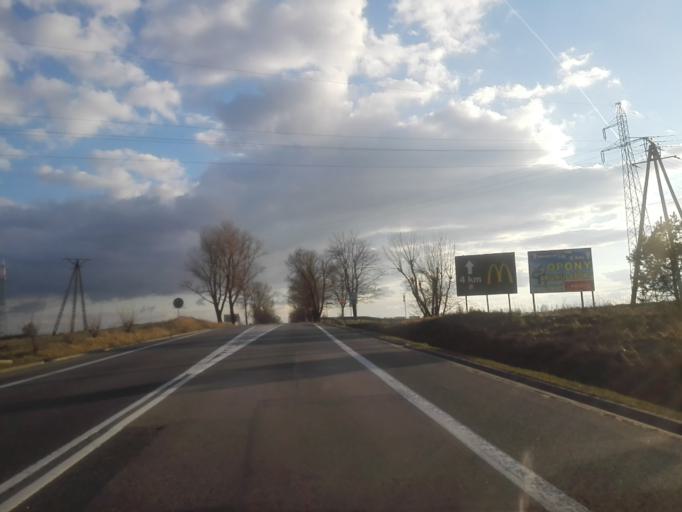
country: PL
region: Podlasie
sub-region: Suwalki
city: Suwalki
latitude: 54.1373
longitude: 22.9571
